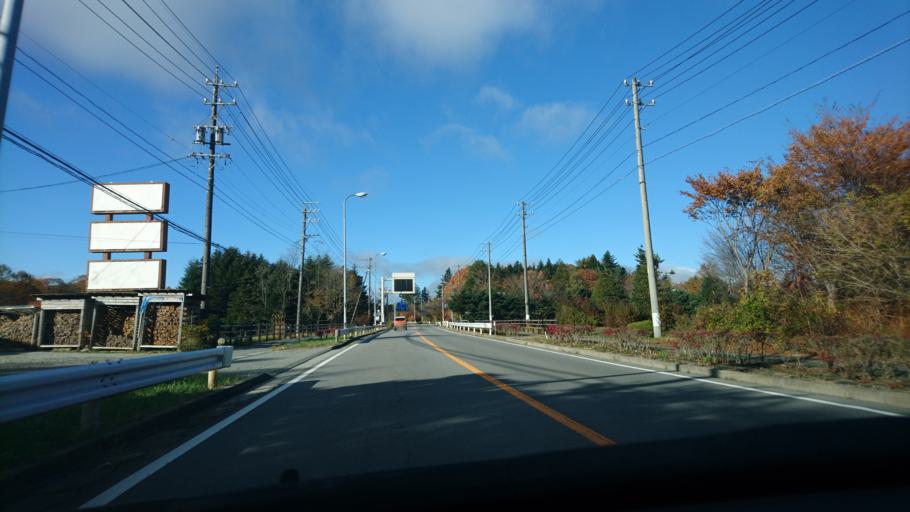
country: JP
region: Nagano
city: Saku
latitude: 36.3259
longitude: 138.6347
